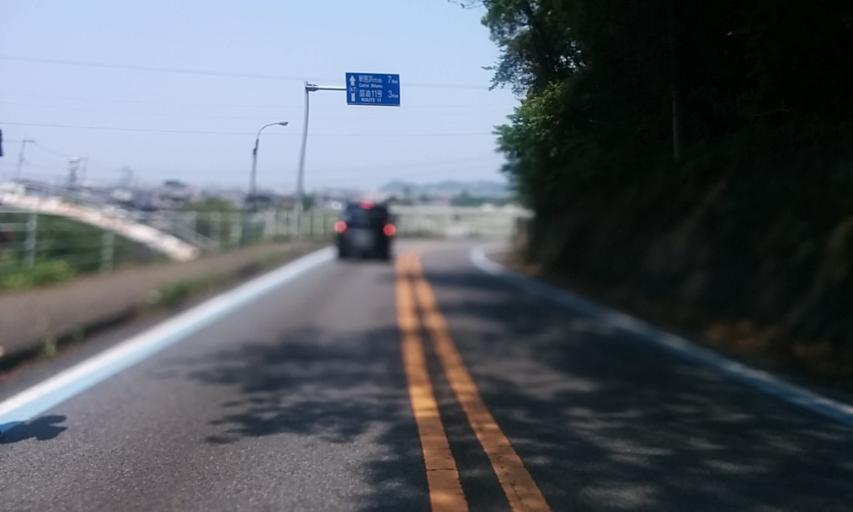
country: JP
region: Ehime
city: Niihama
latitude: 33.9205
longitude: 133.3086
